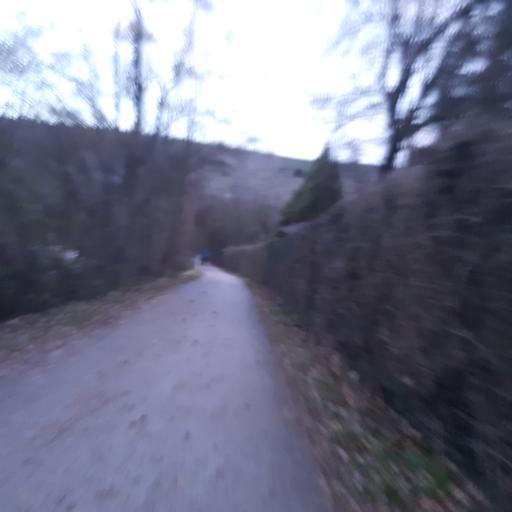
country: DE
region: Baden-Wuerttemberg
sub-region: Regierungsbezirk Stuttgart
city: Mundelsheim
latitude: 49.0014
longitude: 9.2013
